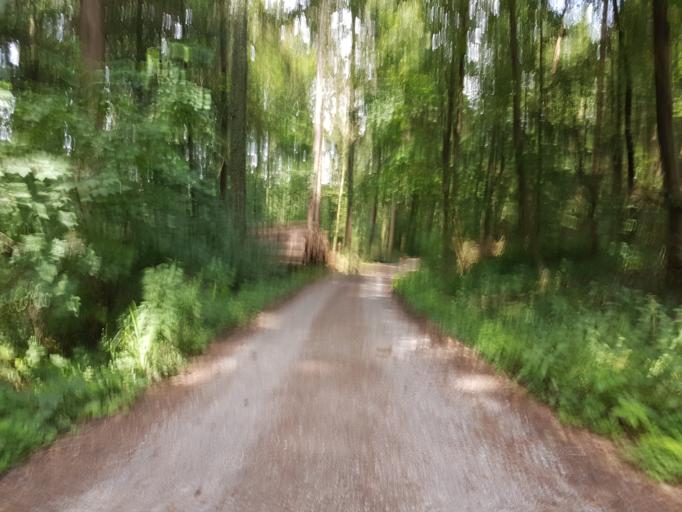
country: DE
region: Baden-Wuerttemberg
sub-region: Regierungsbezirk Stuttgart
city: Zaberfeld
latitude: 49.0440
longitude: 8.9449
